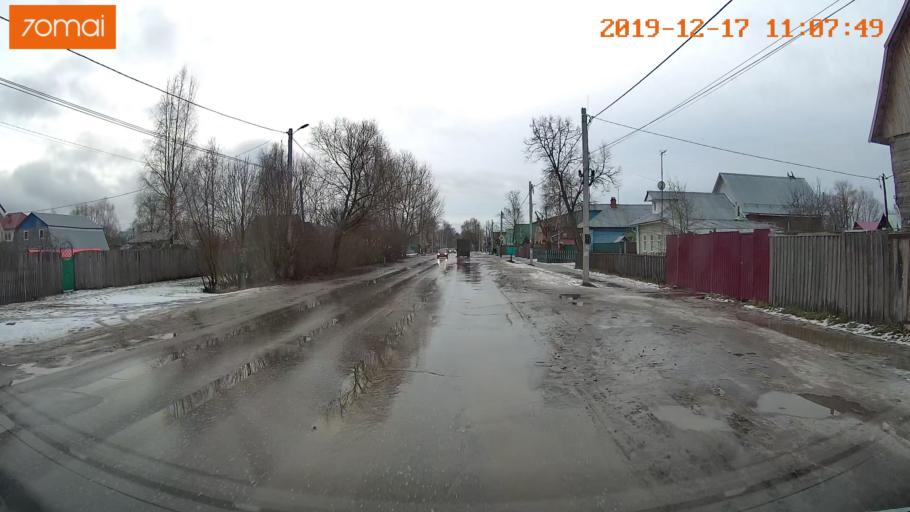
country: RU
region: Vladimir
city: Gus'-Khrustal'nyy
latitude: 55.6087
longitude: 40.6435
